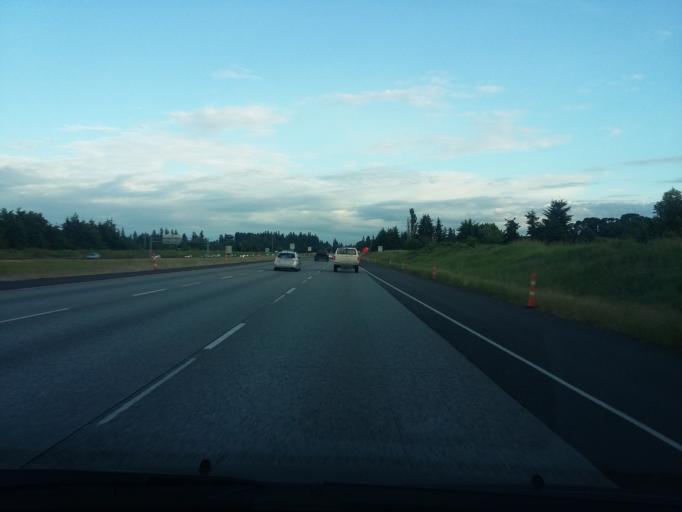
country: US
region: Washington
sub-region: Clark County
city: Orchards
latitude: 45.6486
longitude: -122.5667
